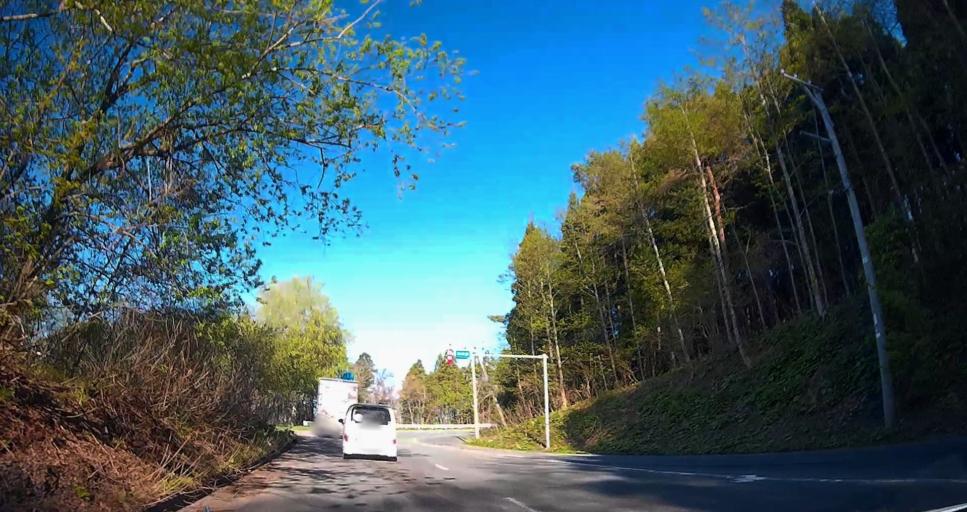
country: JP
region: Aomori
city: Mutsu
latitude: 41.4343
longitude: 141.1327
